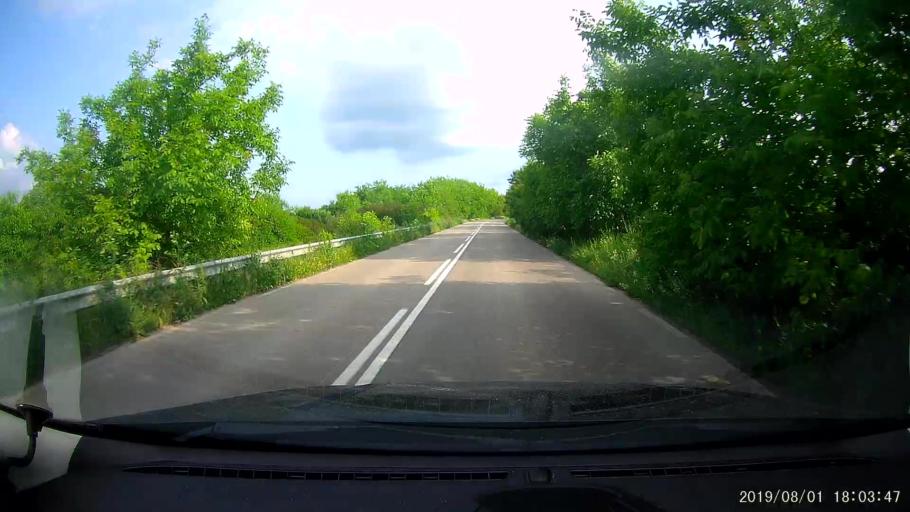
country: BG
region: Silistra
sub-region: Obshtina Alfatar
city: Alfatar
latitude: 43.9194
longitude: 27.2900
